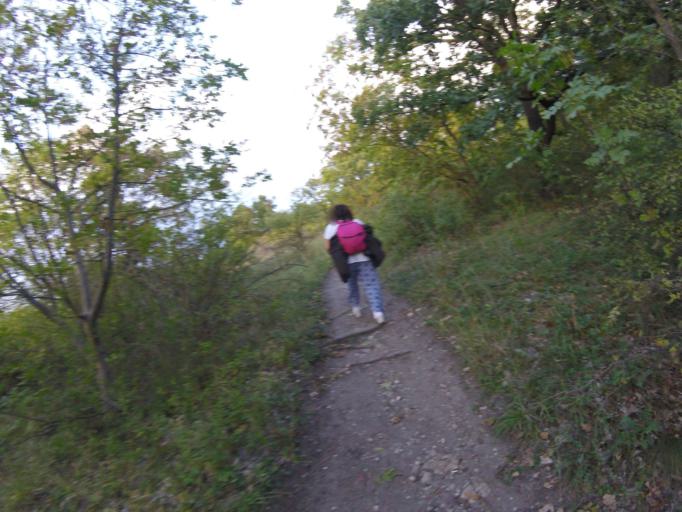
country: HU
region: Pest
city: Fot
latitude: 47.6280
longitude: 19.2113
